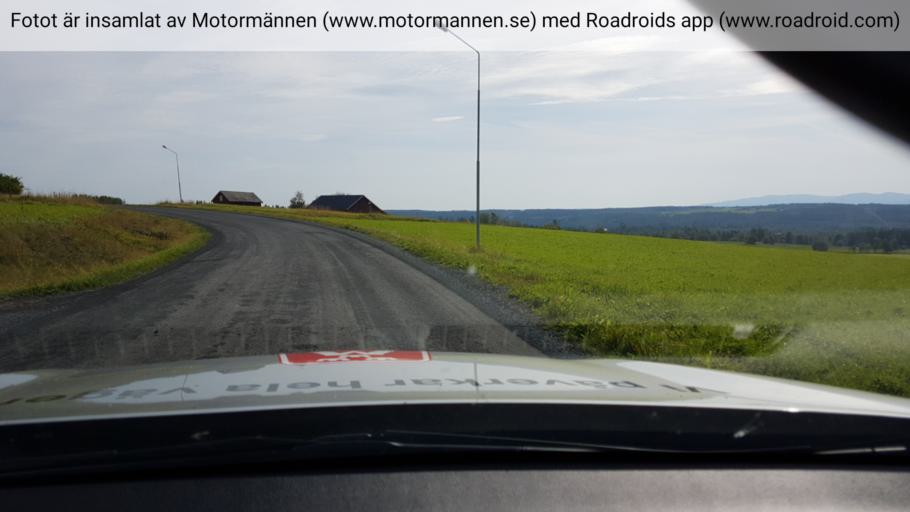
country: SE
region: Jaemtland
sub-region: Krokoms Kommun
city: Valla
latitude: 63.3527
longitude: 13.9825
